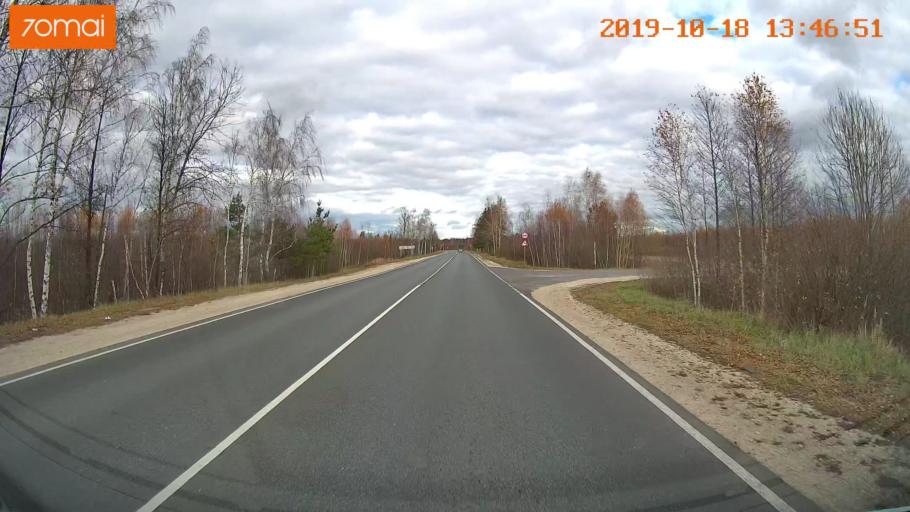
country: RU
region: Rjazan
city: Solotcha
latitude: 54.9666
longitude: 39.9481
